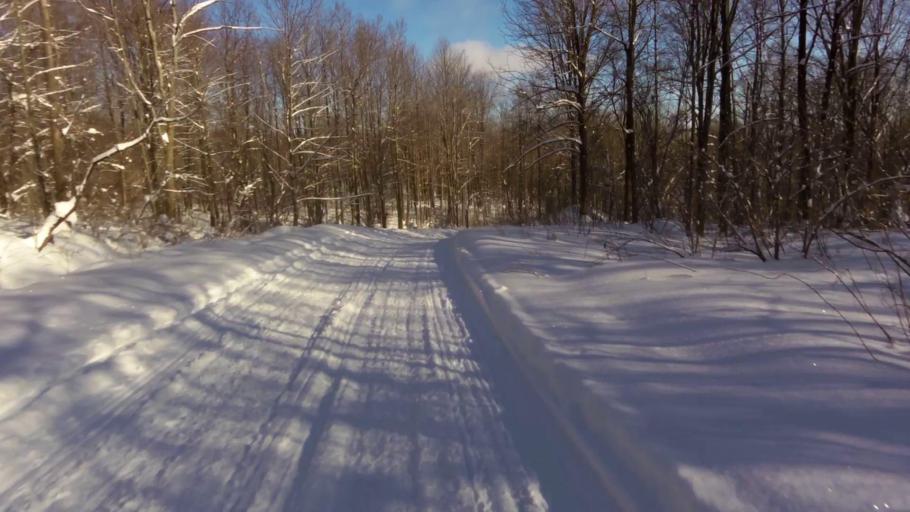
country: US
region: New York
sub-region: Chautauqua County
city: Falconer
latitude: 42.2812
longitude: -79.1279
